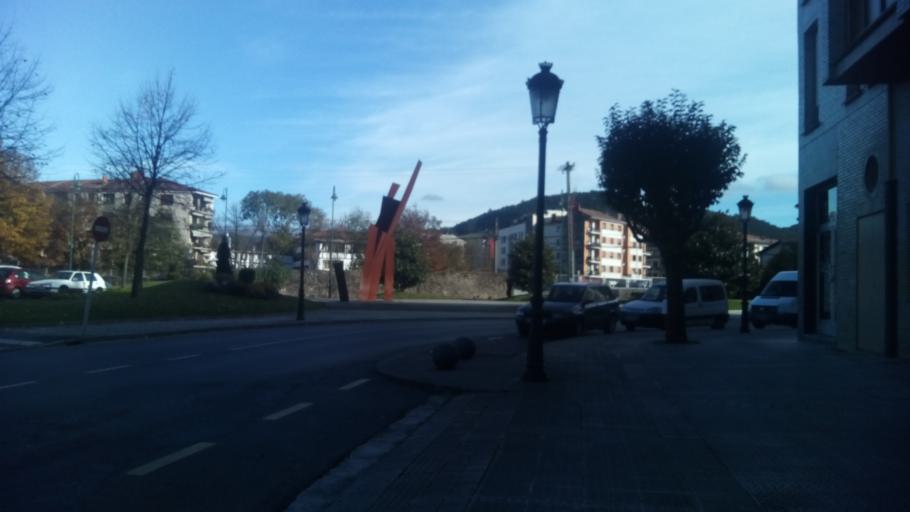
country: ES
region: Basque Country
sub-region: Bizkaia
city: Gernika-Lumo
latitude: 43.3179
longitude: -2.6775
